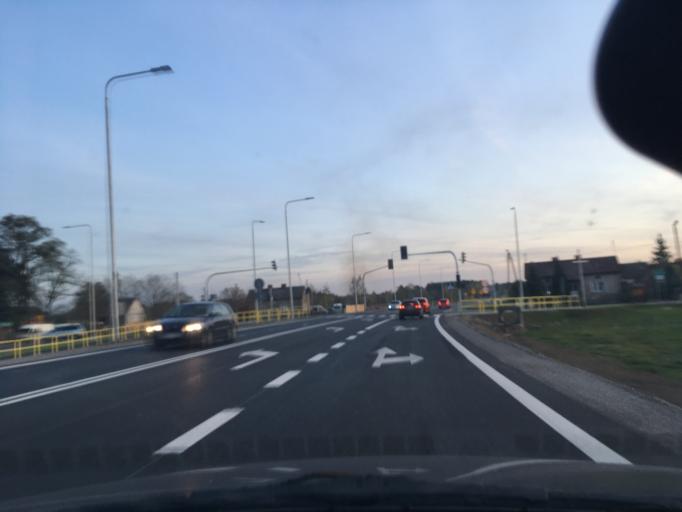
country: PL
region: Masovian Voivodeship
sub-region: Powiat plocki
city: Wyszogrod
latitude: 52.3573
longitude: 20.2083
